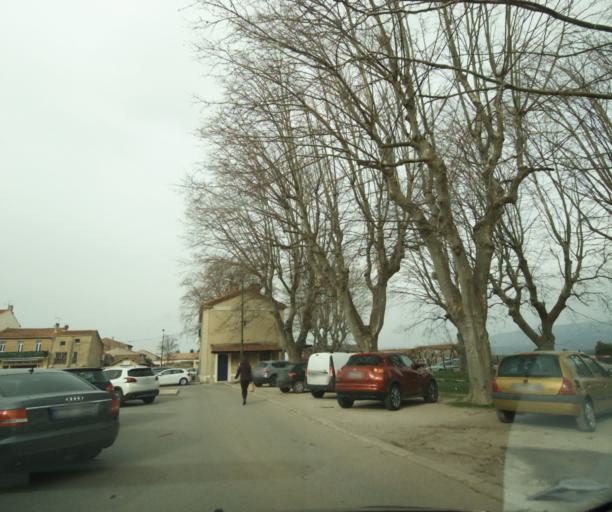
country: FR
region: Provence-Alpes-Cote d'Azur
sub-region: Departement des Bouches-du-Rhone
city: Trets
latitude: 43.4489
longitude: 5.6879
